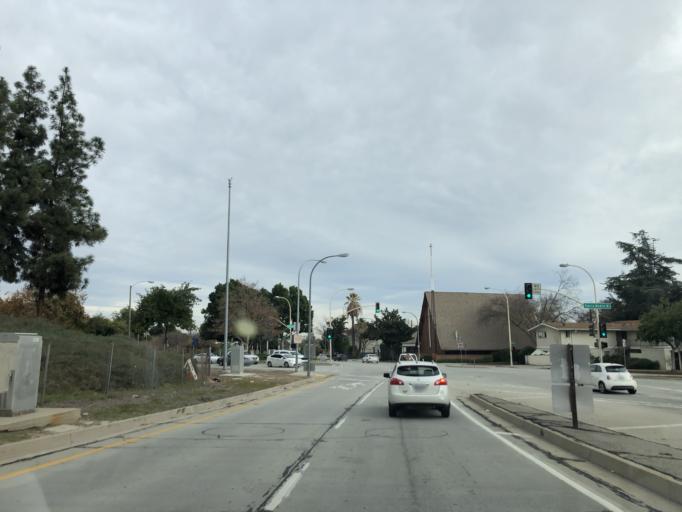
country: US
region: California
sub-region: Los Angeles County
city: East Pasadena
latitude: 34.1520
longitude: -118.0965
